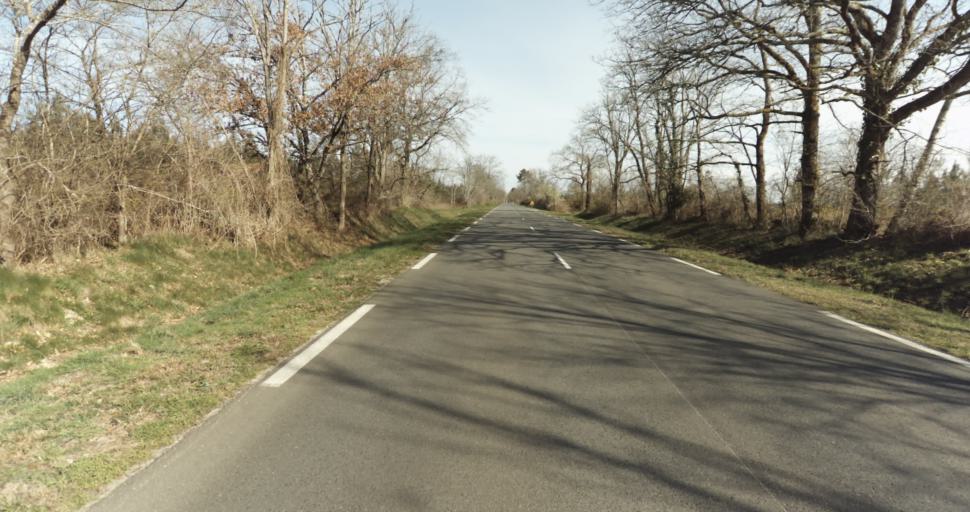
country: FR
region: Aquitaine
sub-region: Departement des Landes
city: Roquefort
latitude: 44.0693
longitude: -0.3150
